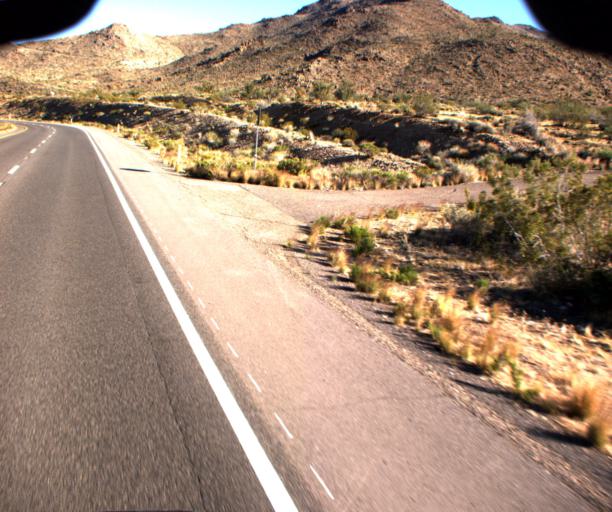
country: US
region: Arizona
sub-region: Mohave County
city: Kingman
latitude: 35.2202
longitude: -114.1208
